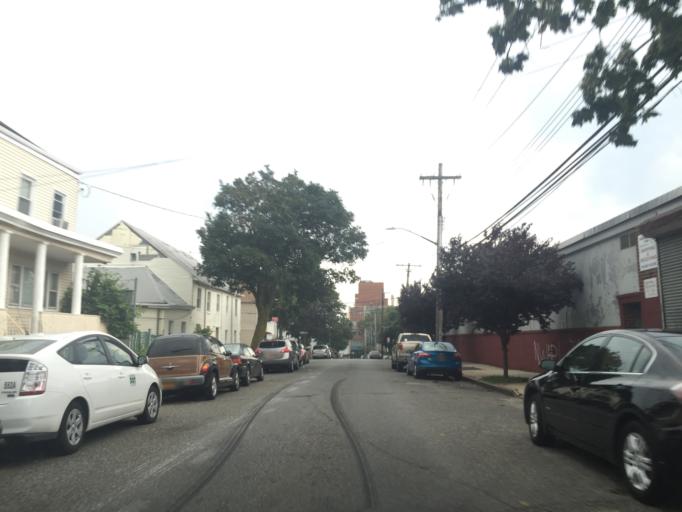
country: US
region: New York
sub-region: Bronx
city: The Bronx
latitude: 40.7846
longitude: -73.8541
